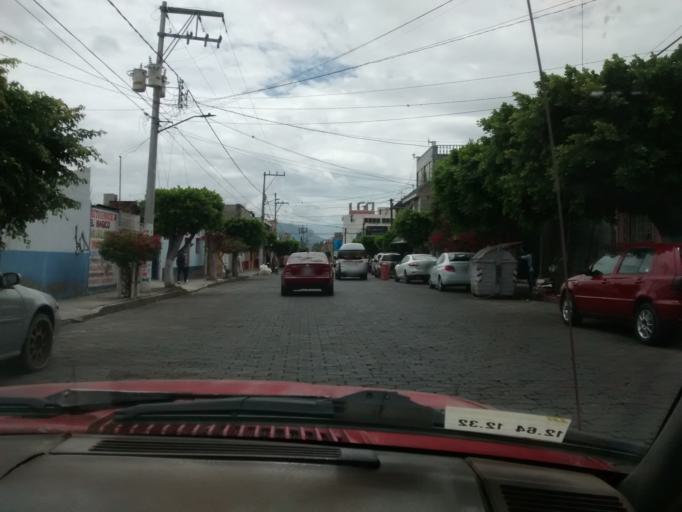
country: MX
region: Puebla
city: Tehuacan
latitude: 18.4673
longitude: -97.3988
